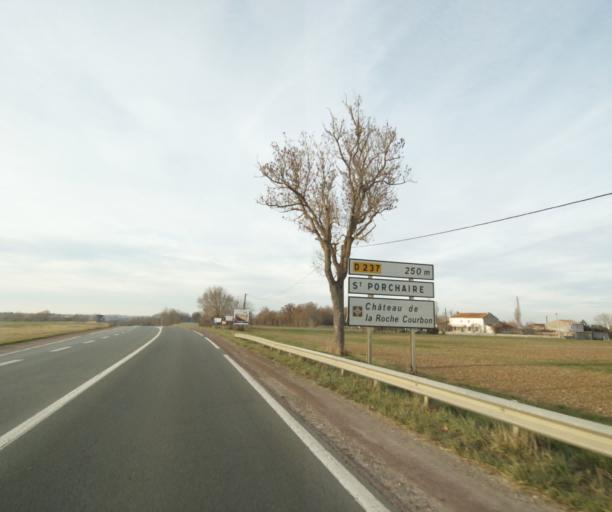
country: FR
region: Poitou-Charentes
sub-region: Departement de la Charente-Maritime
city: Saint-Porchaire
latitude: 45.8099
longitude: -0.7625
